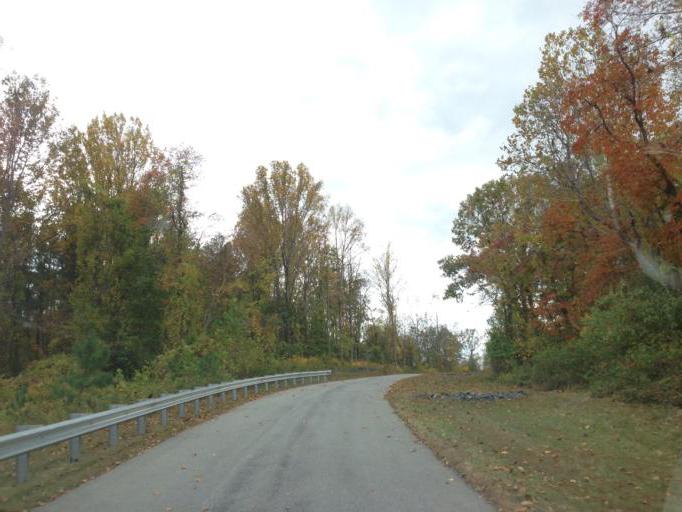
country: US
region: Maryland
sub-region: Montgomery County
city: Olney
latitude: 39.2534
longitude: -77.0480
